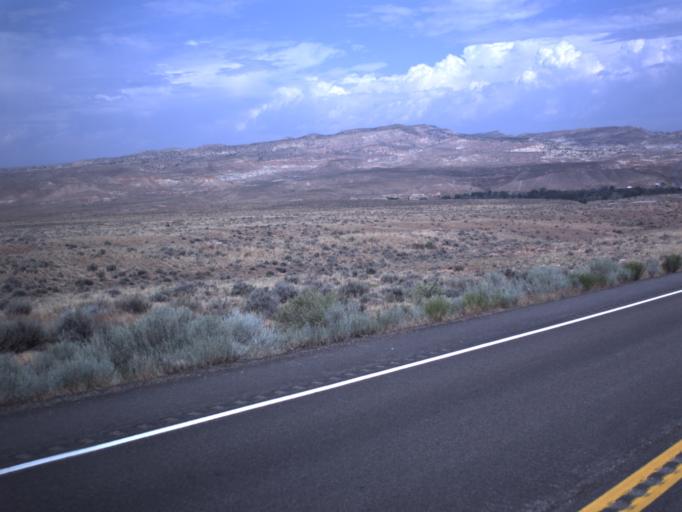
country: US
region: Utah
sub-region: Uintah County
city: Naples
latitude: 40.2976
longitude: -109.4769
